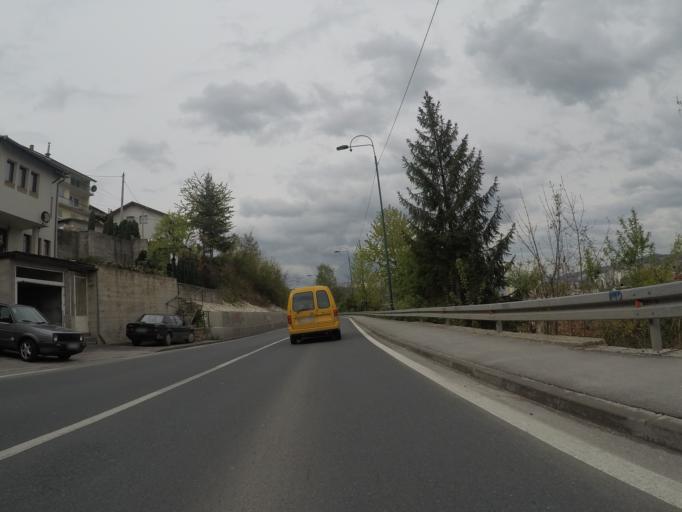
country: BA
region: Federation of Bosnia and Herzegovina
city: Kobilja Glava
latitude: 43.8507
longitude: 18.4061
